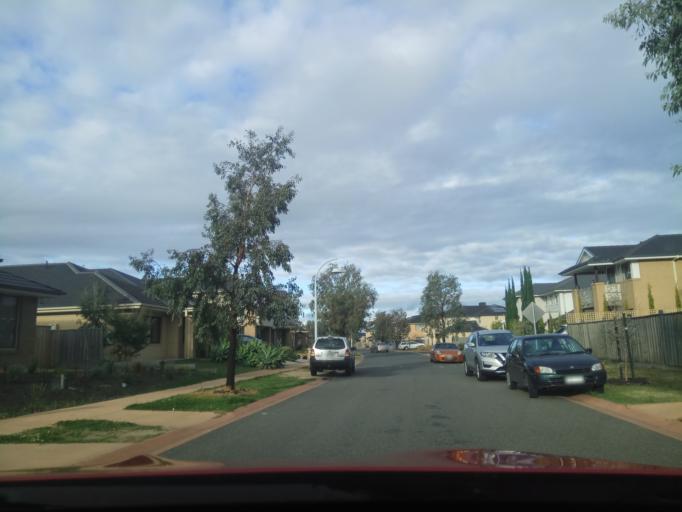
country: AU
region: Victoria
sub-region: Wyndham
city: Point Cook
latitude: -37.9065
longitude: 144.7670
